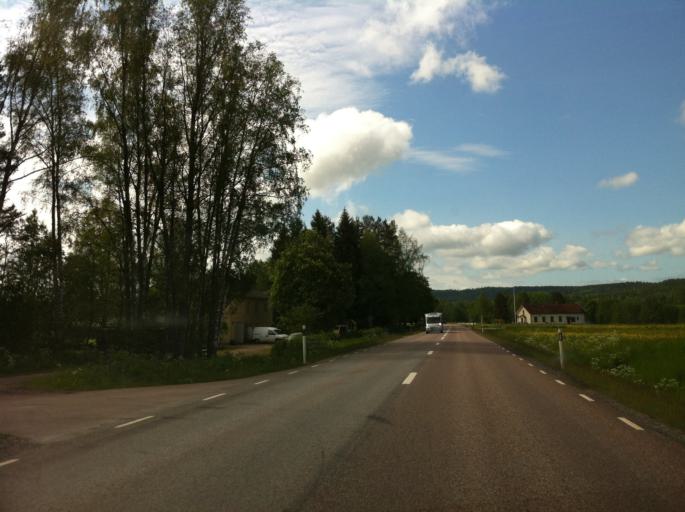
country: SE
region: Vaermland
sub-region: Sunne Kommun
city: Sunne
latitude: 59.6918
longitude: 13.1412
